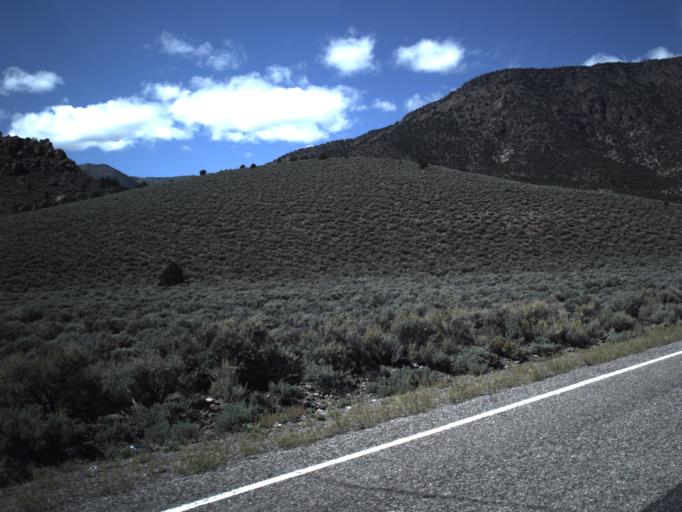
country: US
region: Utah
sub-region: Piute County
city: Junction
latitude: 38.2599
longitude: -112.2482
